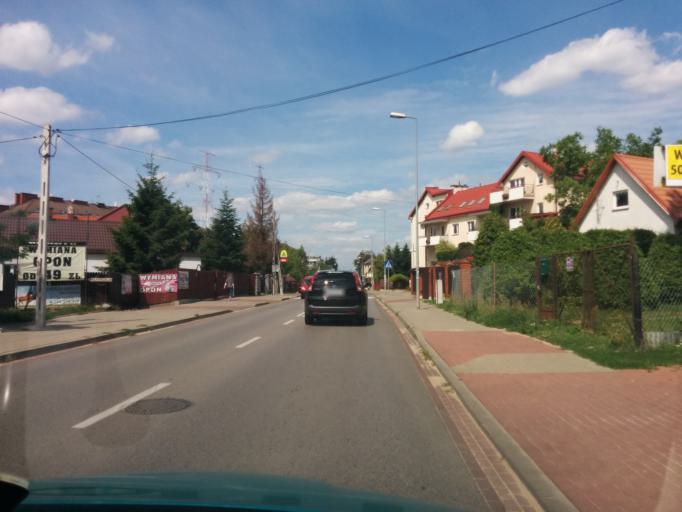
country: PL
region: Masovian Voivodeship
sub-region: Warszawa
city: Bielany
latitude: 52.3209
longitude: 20.9403
